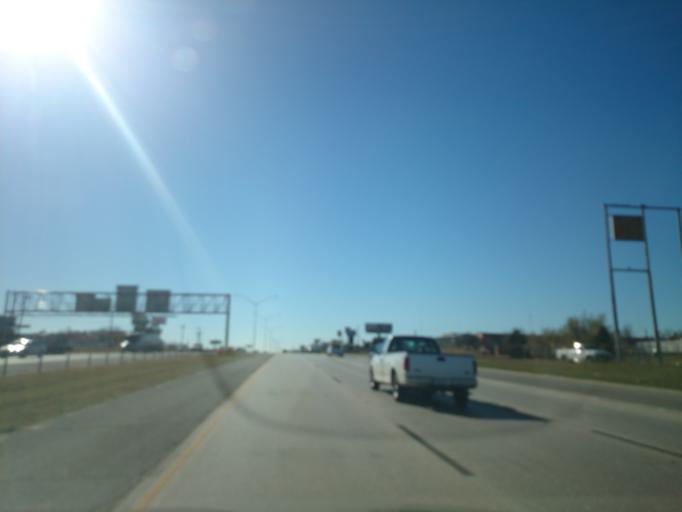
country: US
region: Oklahoma
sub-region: Oklahoma County
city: Edmond
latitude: 35.5910
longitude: -97.4353
